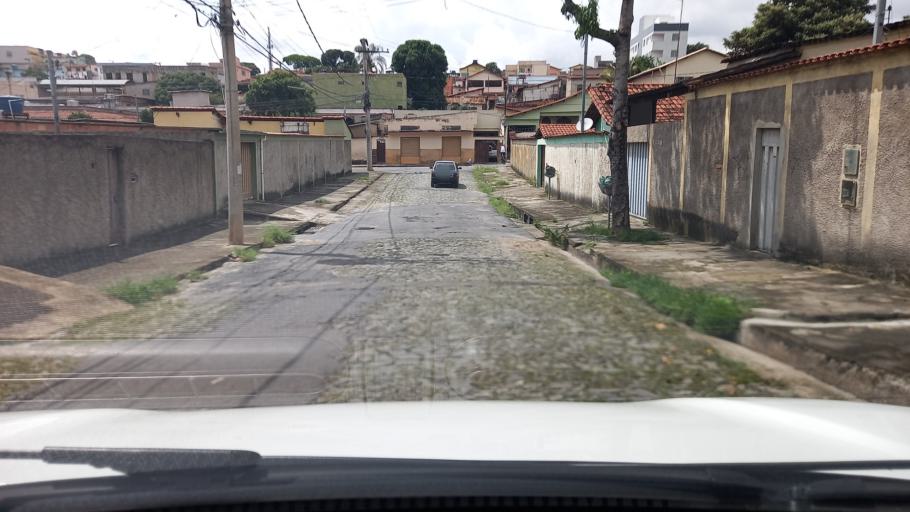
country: BR
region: Minas Gerais
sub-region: Contagem
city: Contagem
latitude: -19.9060
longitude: -44.0256
